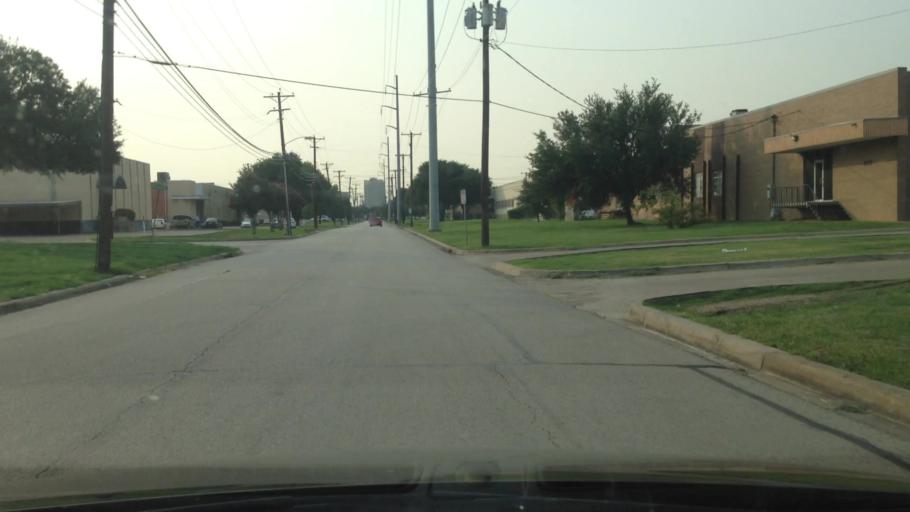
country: US
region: Texas
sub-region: Dallas County
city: Irving
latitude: 32.8274
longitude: -96.8817
